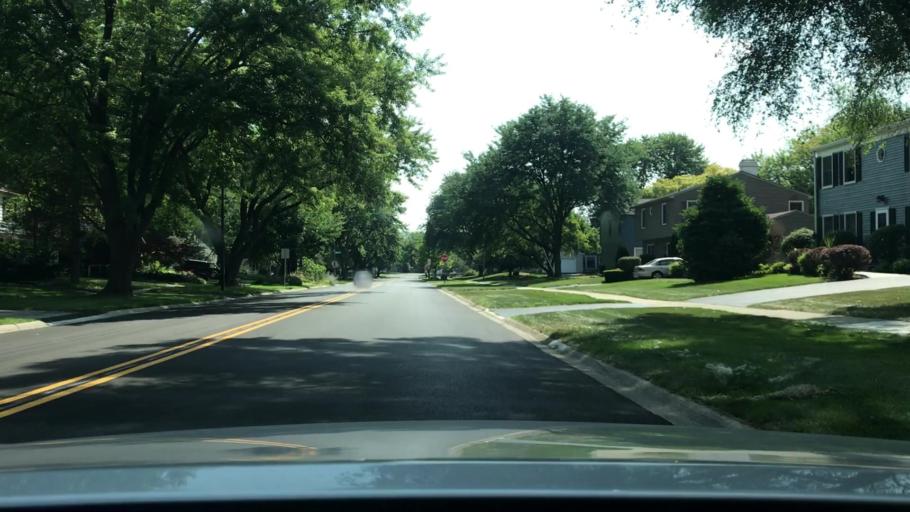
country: US
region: Illinois
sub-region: DuPage County
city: Naperville
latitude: 41.7412
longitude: -88.1366
